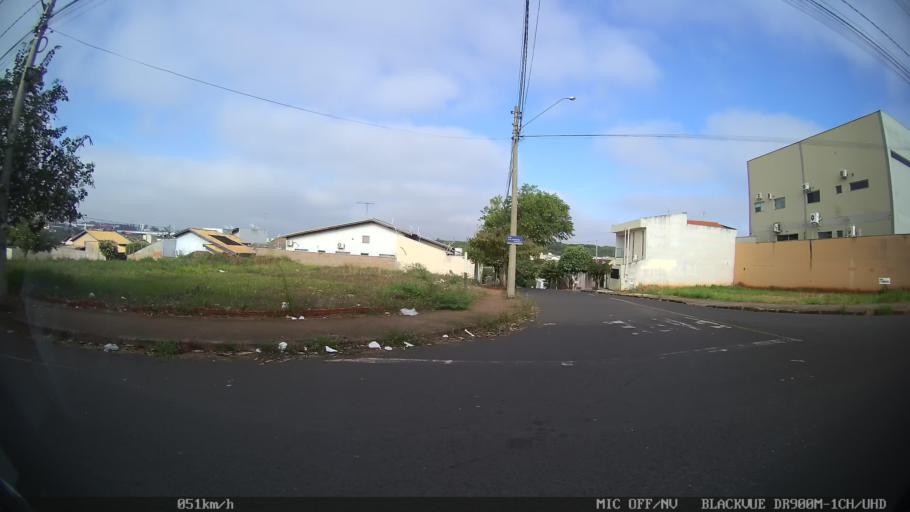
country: BR
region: Sao Paulo
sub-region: Sao Jose Do Rio Preto
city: Sao Jose do Rio Preto
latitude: -20.8027
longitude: -49.4295
